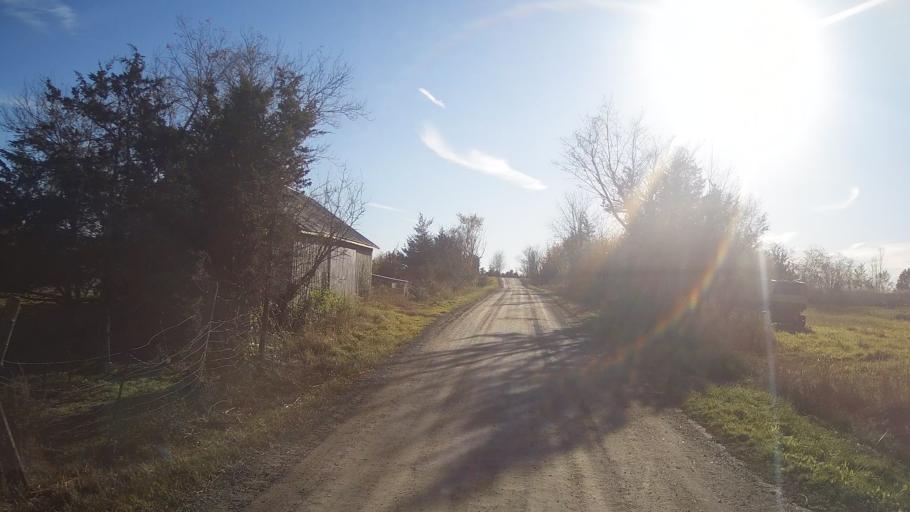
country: CA
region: Ontario
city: Perth
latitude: 44.7077
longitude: -76.4259
